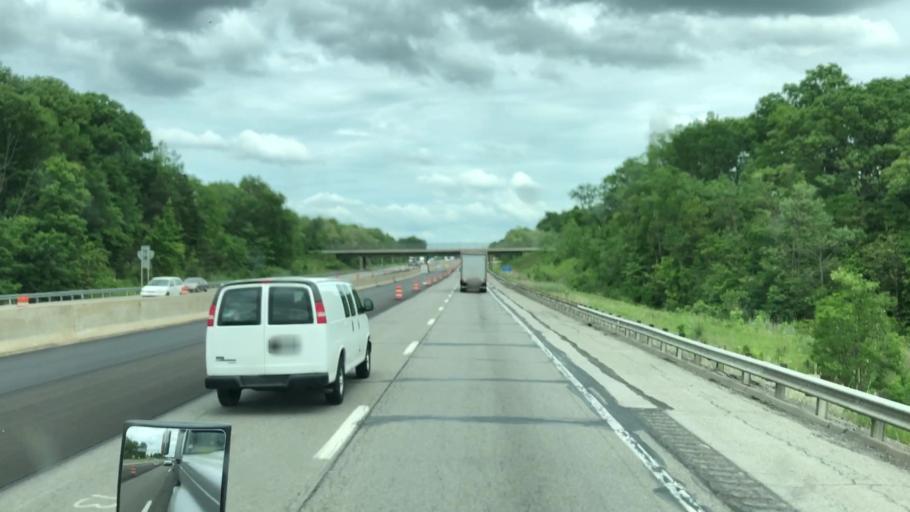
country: US
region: Ohio
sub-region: Lorain County
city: South Amherst
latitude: 41.3559
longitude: -82.2950
